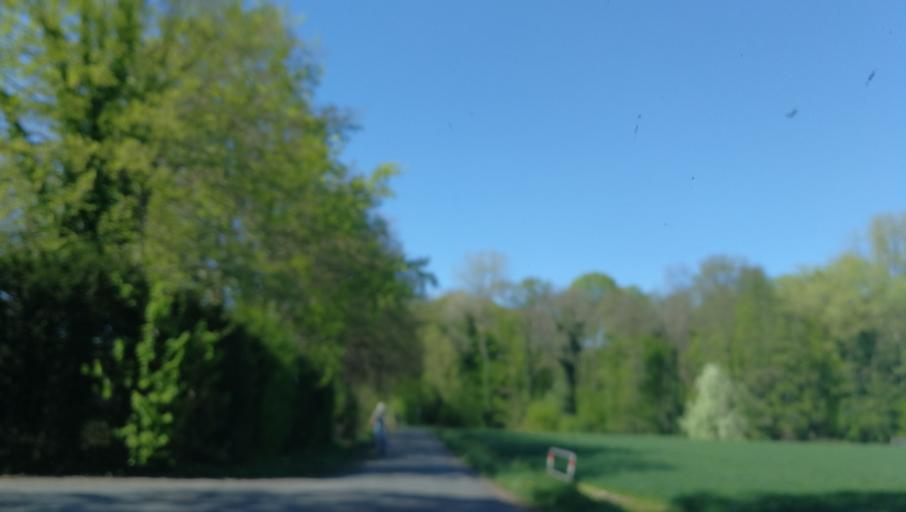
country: DE
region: North Rhine-Westphalia
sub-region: Regierungsbezirk Munster
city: Muenster
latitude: 51.9389
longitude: 7.5466
